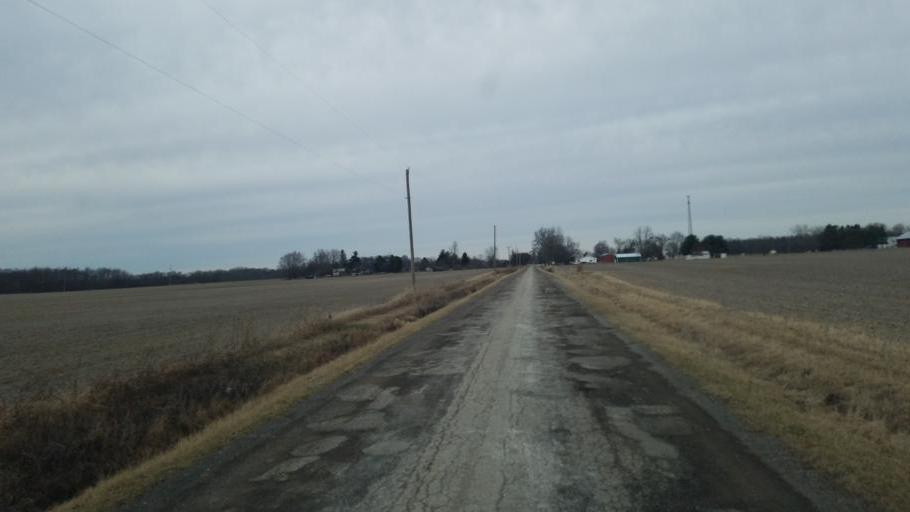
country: US
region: Ohio
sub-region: Morrow County
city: Cardington
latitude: 40.4636
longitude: -82.9306
